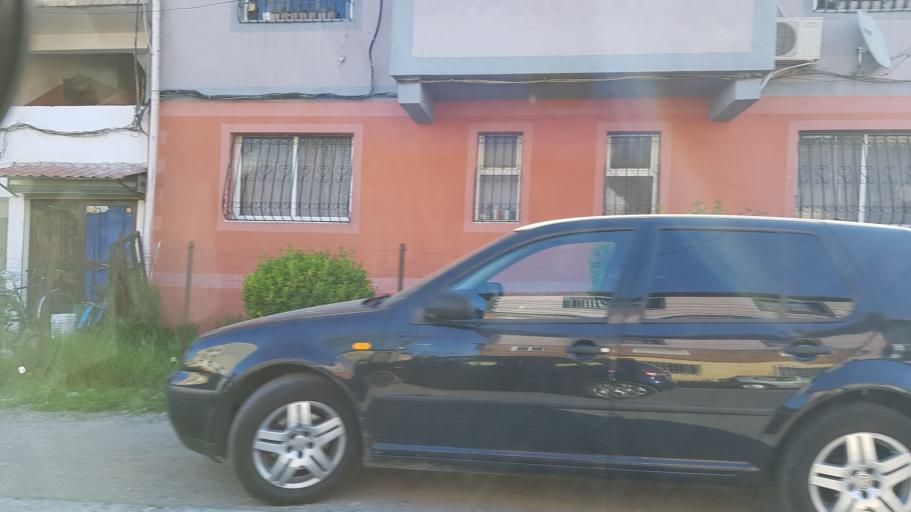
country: AL
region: Shkoder
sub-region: Rrethi i Shkodres
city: Shkoder
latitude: 42.0596
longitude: 19.5140
